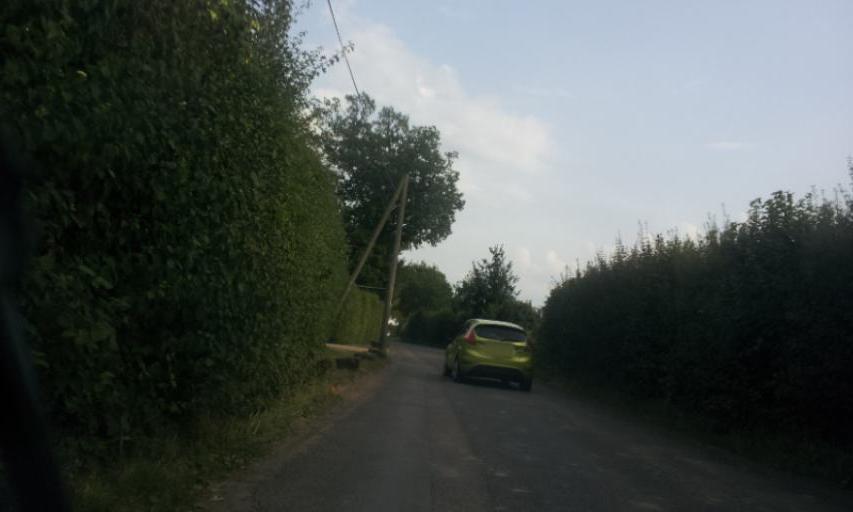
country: GB
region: England
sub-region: Kent
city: Paddock Wood
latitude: 51.1688
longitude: 0.4010
